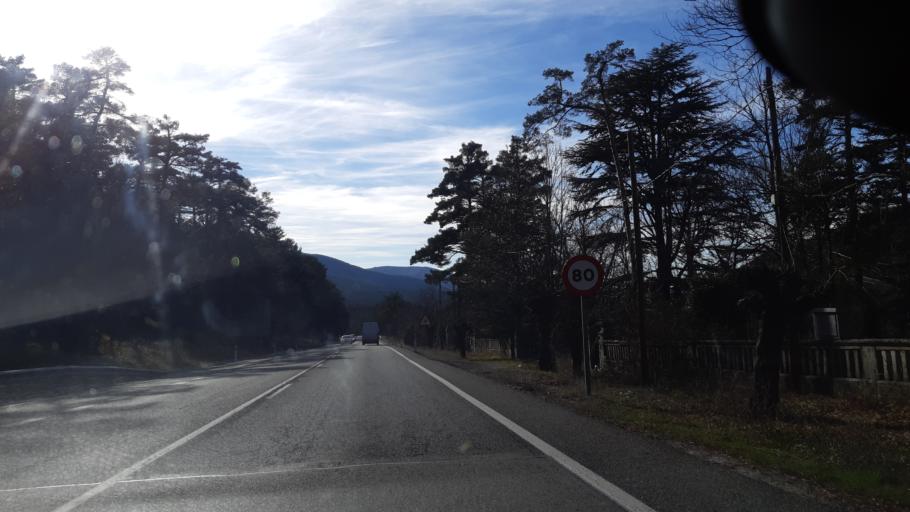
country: ES
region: Madrid
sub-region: Provincia de Madrid
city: Guadarrama
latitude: 40.7126
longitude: -4.1613
